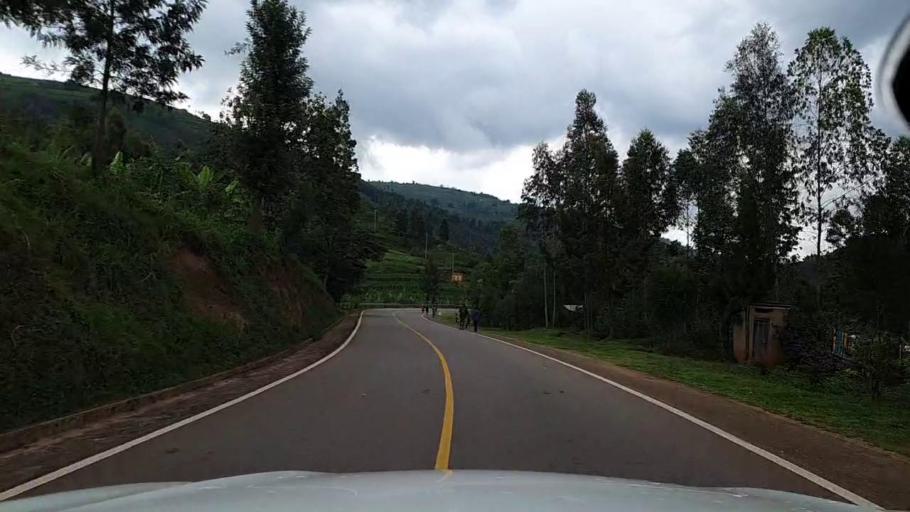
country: RW
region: Northern Province
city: Byumba
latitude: -1.6772
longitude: 30.0988
